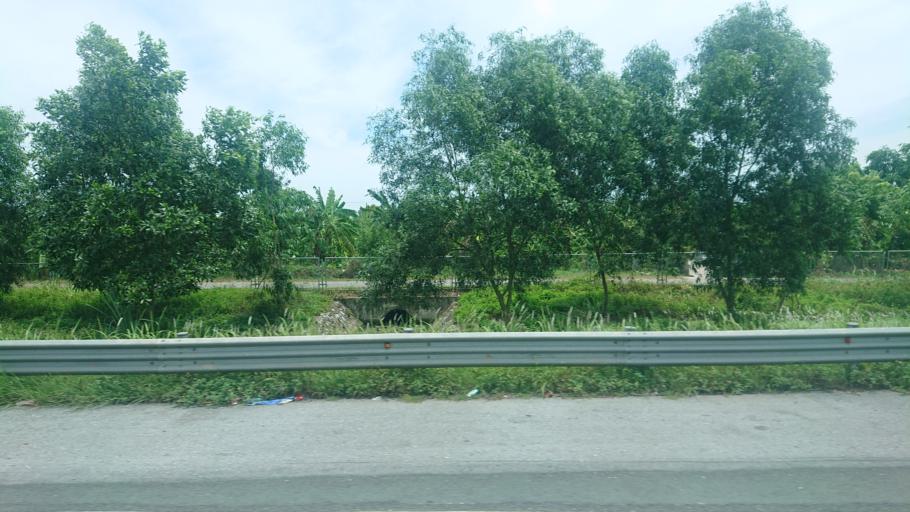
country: VN
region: Hai Phong
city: An Lao
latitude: 20.8164
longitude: 106.4896
